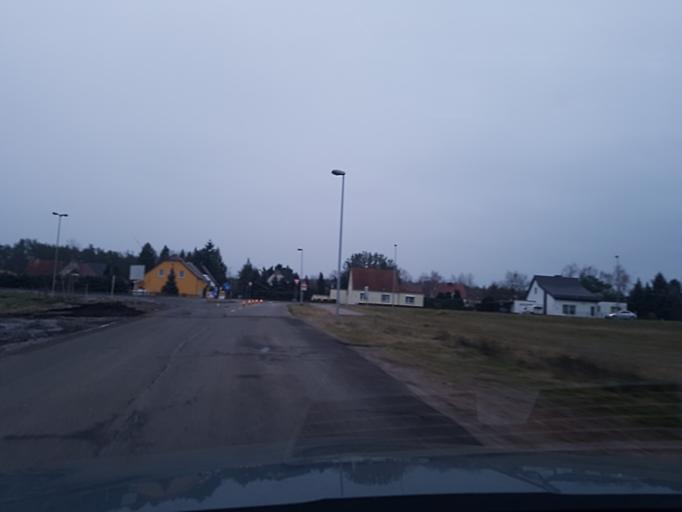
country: DE
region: Brandenburg
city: Doberlug-Kirchhain
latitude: 51.6285
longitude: 13.5839
